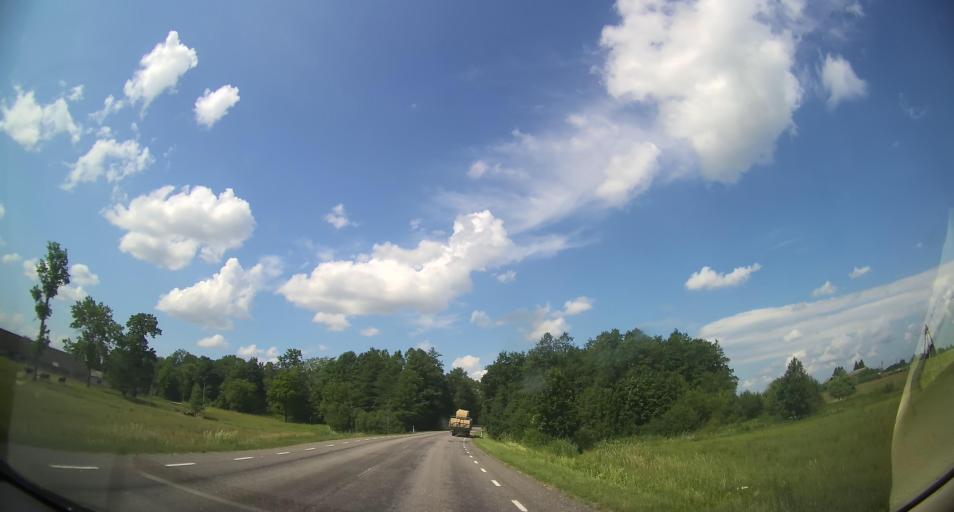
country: EE
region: Raplamaa
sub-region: Maerjamaa vald
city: Marjamaa
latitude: 58.8945
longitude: 24.2455
